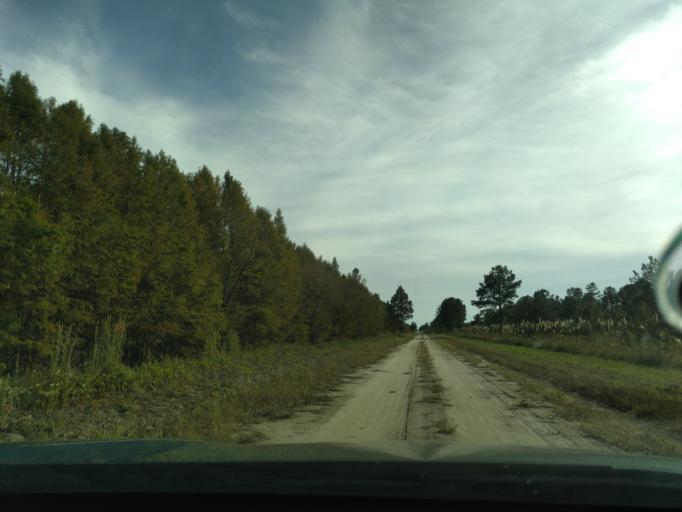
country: US
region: North Carolina
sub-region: Beaufort County
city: Belhaven
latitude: 35.6857
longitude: -76.5441
